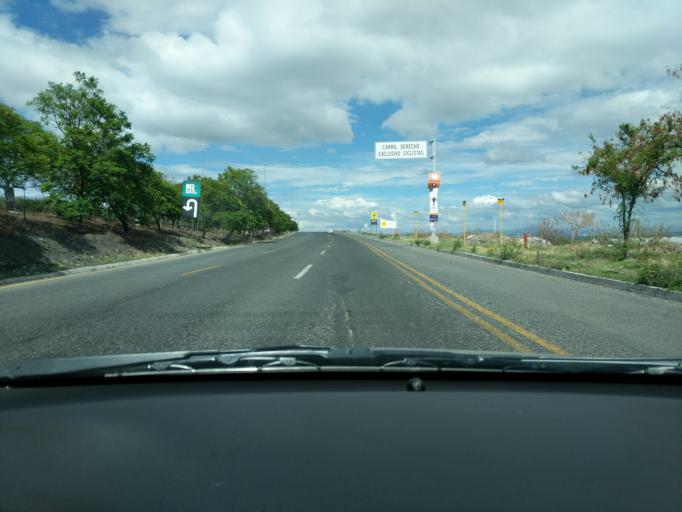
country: MX
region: Queretaro
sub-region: El Marques
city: La Pradera
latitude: 20.6624
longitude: -100.3383
